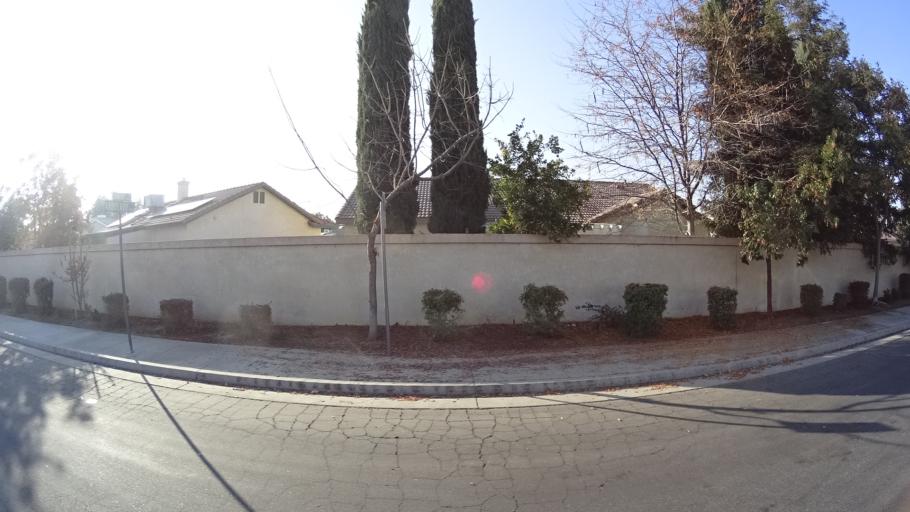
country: US
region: California
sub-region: Kern County
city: Rosedale
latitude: 35.3568
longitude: -119.1544
